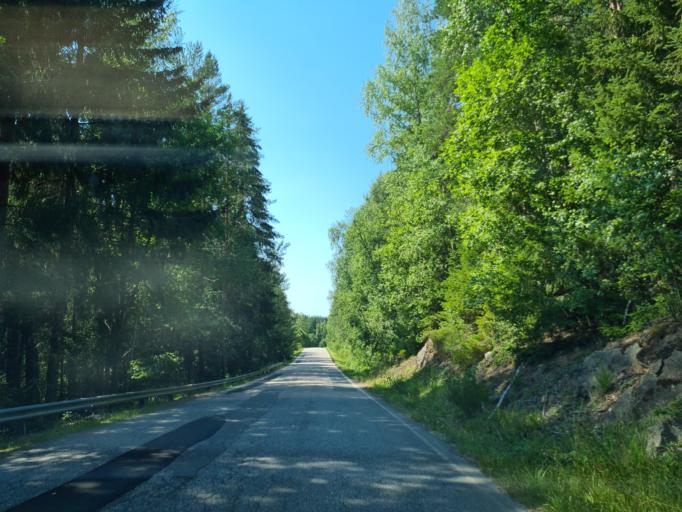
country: FI
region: Varsinais-Suomi
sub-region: Loimaa
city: Aura
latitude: 60.6036
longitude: 22.5817
